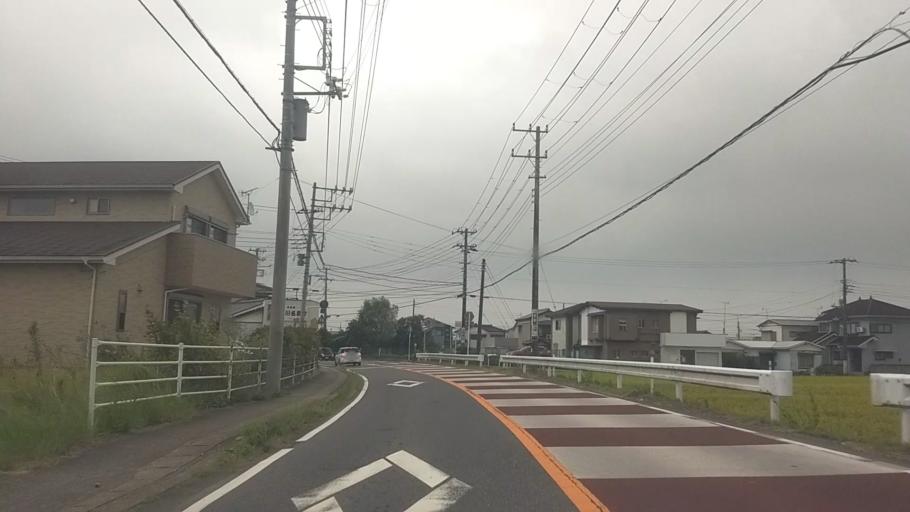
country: JP
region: Chiba
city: Kawaguchi
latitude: 35.1131
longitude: 140.0946
